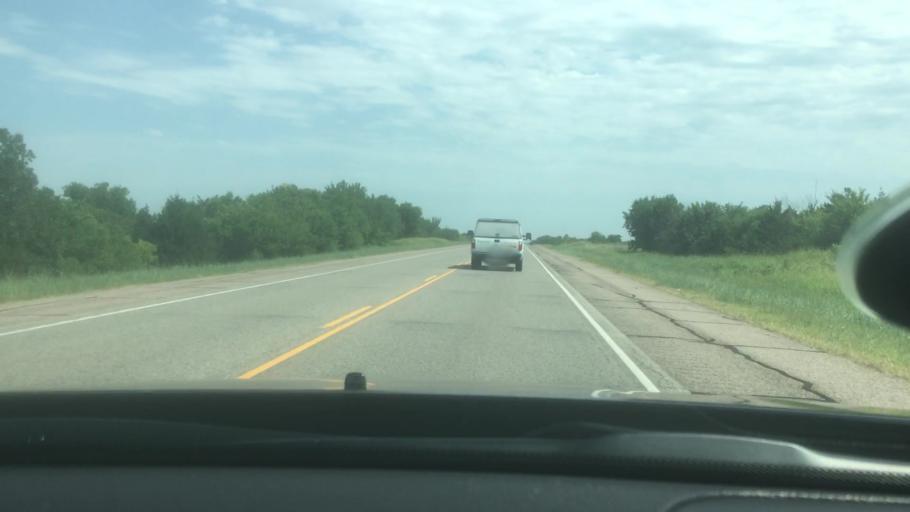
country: US
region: Oklahoma
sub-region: Seminole County
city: Maud
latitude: 35.0395
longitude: -96.9314
